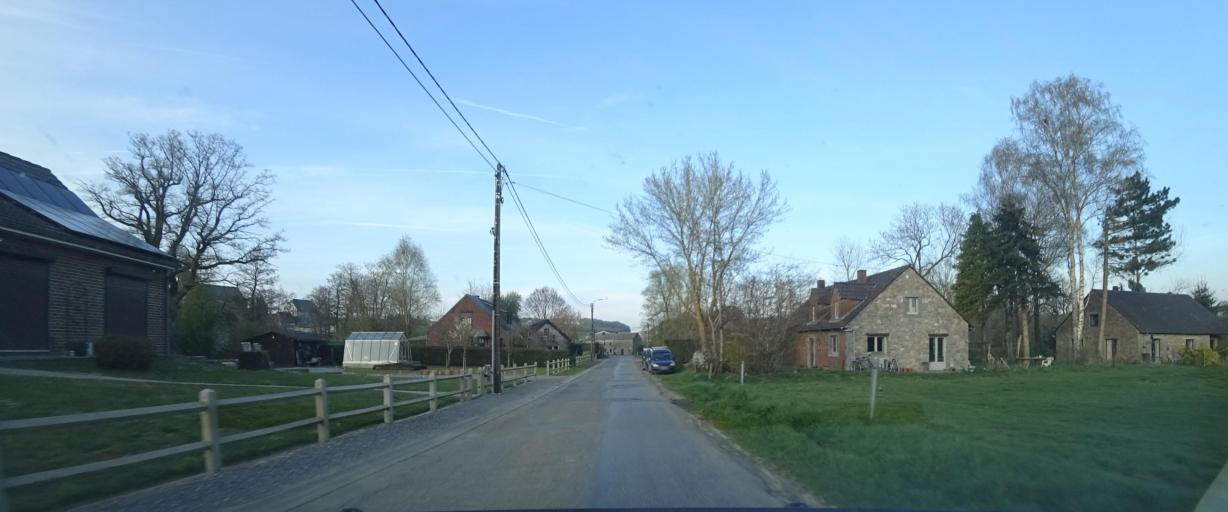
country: BE
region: Wallonia
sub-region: Province de Namur
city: Hamois
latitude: 50.3176
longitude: 5.1907
